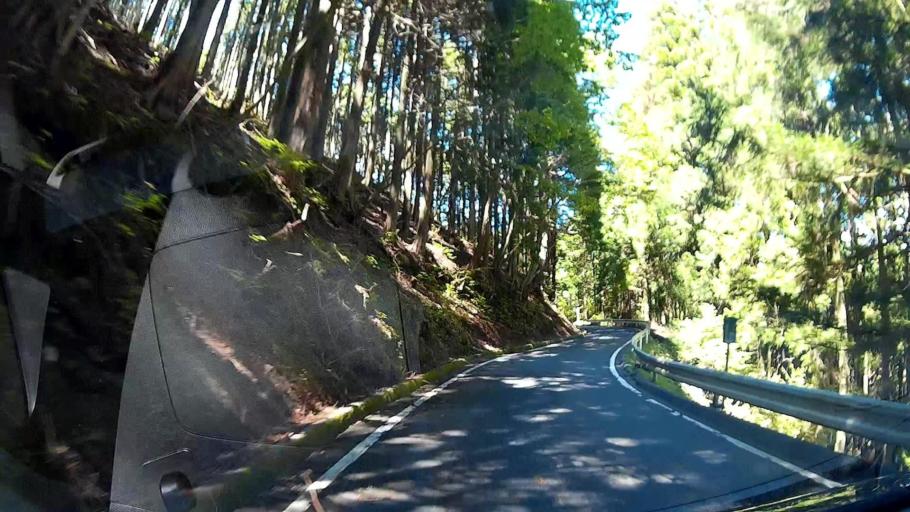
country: JP
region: Shizuoka
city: Shizuoka-shi
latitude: 35.1951
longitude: 138.2596
